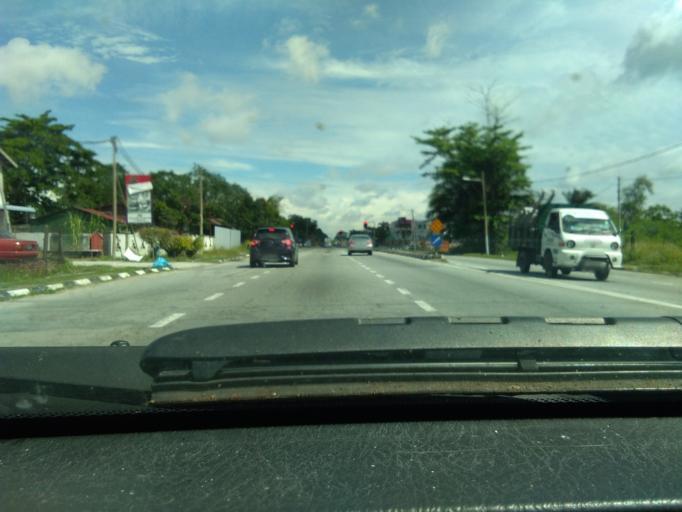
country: MY
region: Perak
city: Parit Buntar
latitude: 5.1100
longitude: 100.4826
